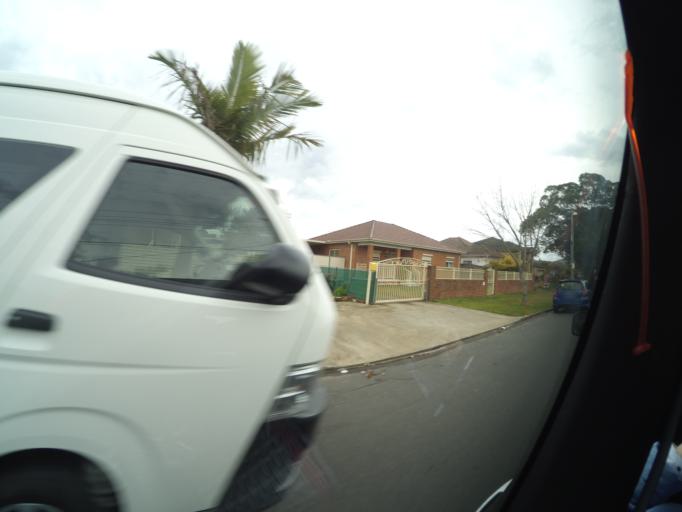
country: AU
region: New South Wales
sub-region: Bankstown
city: Bankstown
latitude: -33.9090
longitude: 151.0202
